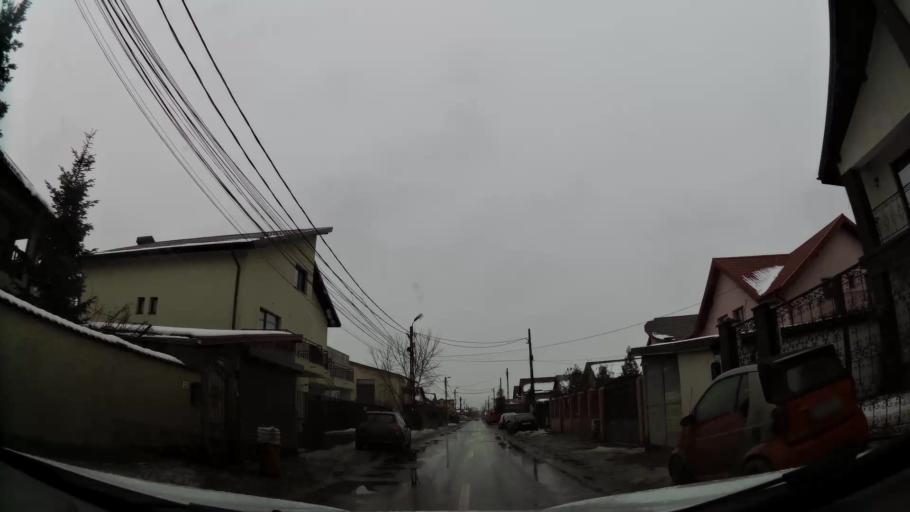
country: RO
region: Ilfov
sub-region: Comuna Bragadiru
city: Bragadiru
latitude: 44.4014
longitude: 26.0097
